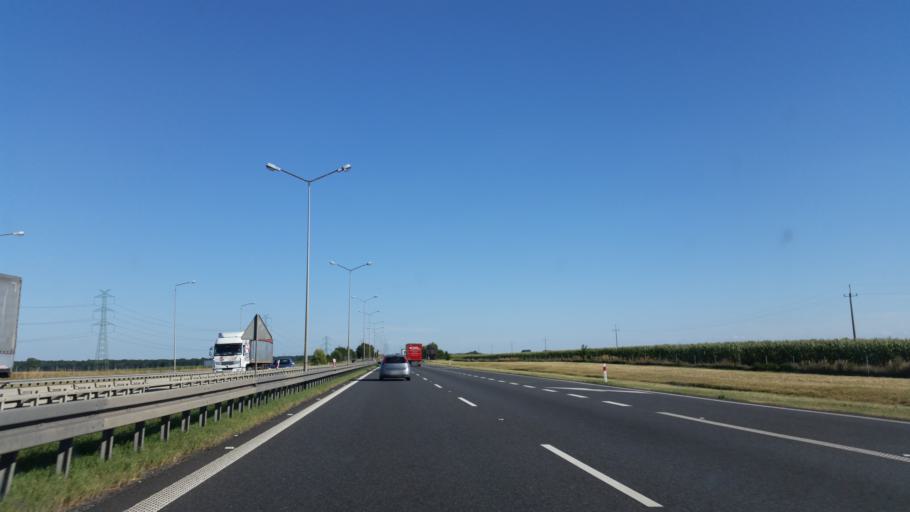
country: PL
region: Lower Silesian Voivodeship
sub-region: Powiat strzelinski
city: Wiazow
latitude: 50.8770
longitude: 17.2048
